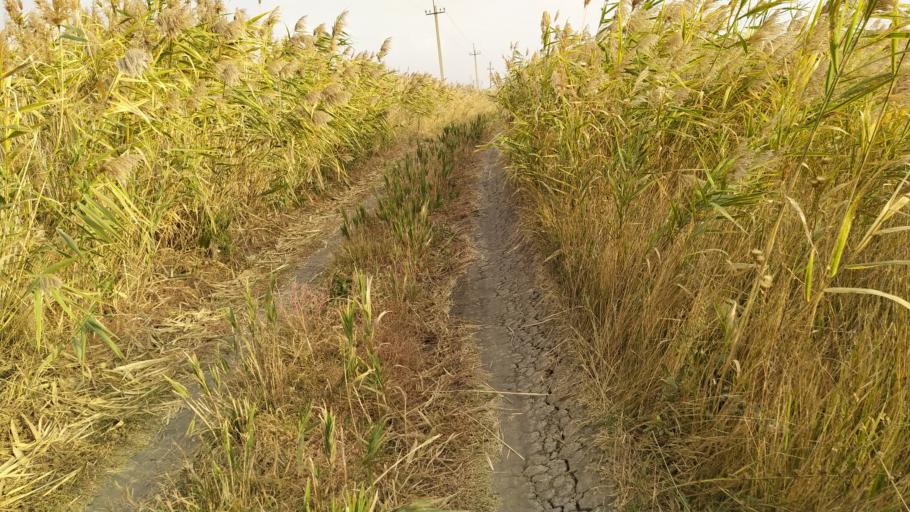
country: RU
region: Rostov
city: Kuleshovka
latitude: 47.1110
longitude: 39.6108
